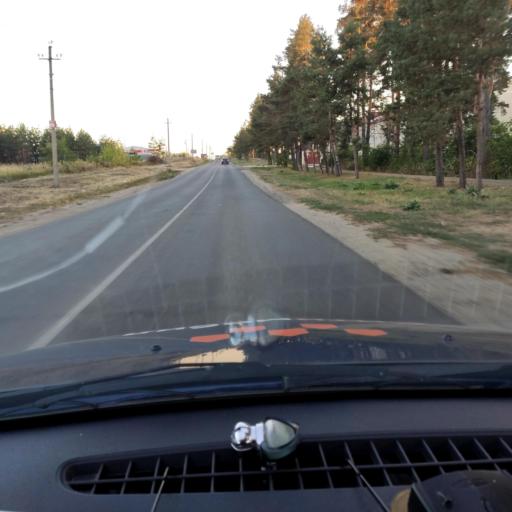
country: RU
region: Voronezj
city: Podgornoye
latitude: 51.8156
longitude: 39.1409
